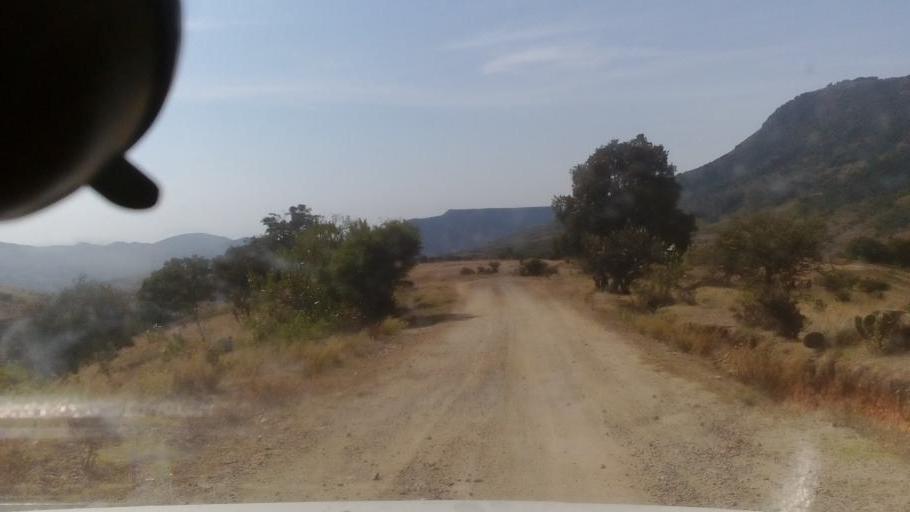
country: MX
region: Guanajuato
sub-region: Leon
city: Lucio Blanco (Los Gavilanes)
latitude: 21.2027
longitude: -101.4984
